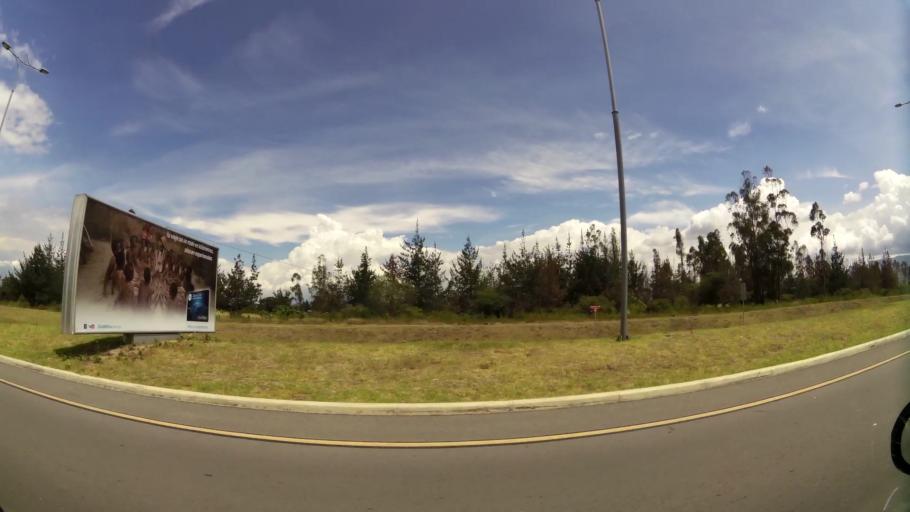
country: EC
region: Pichincha
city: Quito
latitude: -0.1434
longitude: -78.3558
